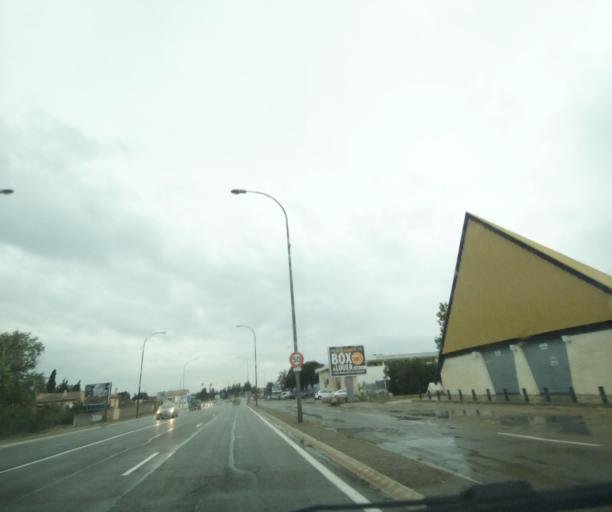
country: FR
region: Languedoc-Roussillon
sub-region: Departement du Gard
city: Rodilhan
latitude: 43.8553
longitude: 4.4028
